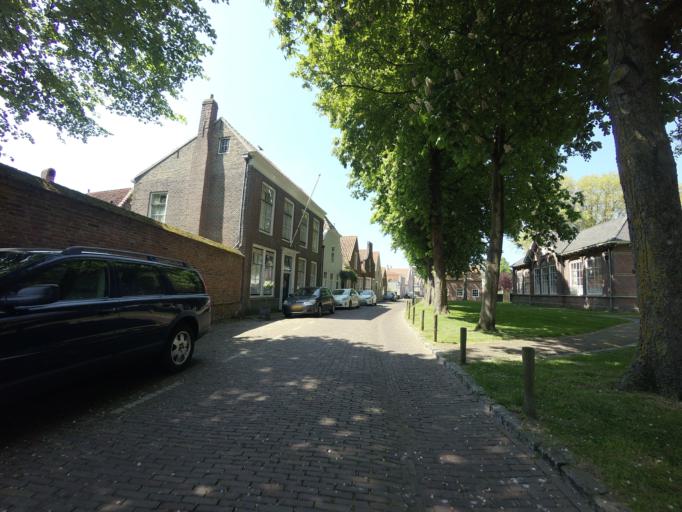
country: NL
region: Zeeland
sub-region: Gemeente Veere
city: Veere
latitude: 51.5476
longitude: 3.6676
